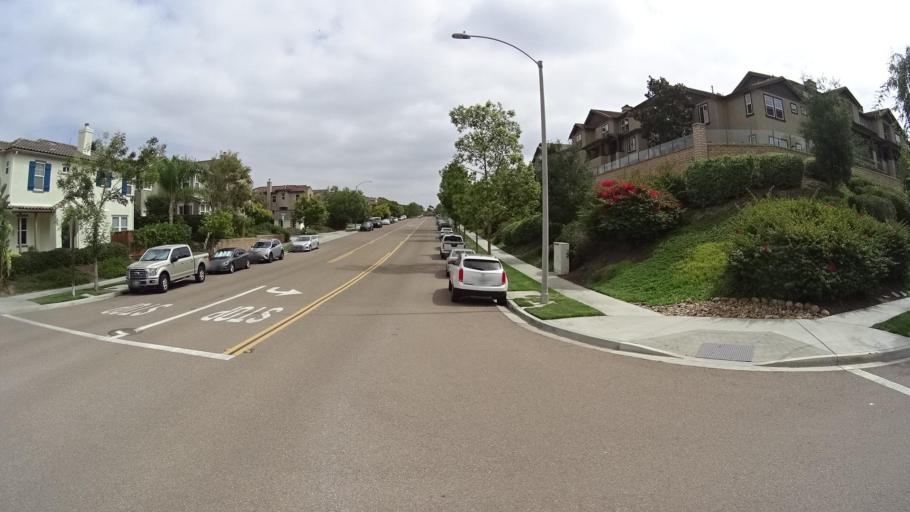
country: US
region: California
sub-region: San Diego County
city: Fairbanks Ranch
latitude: 33.0245
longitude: -117.1143
